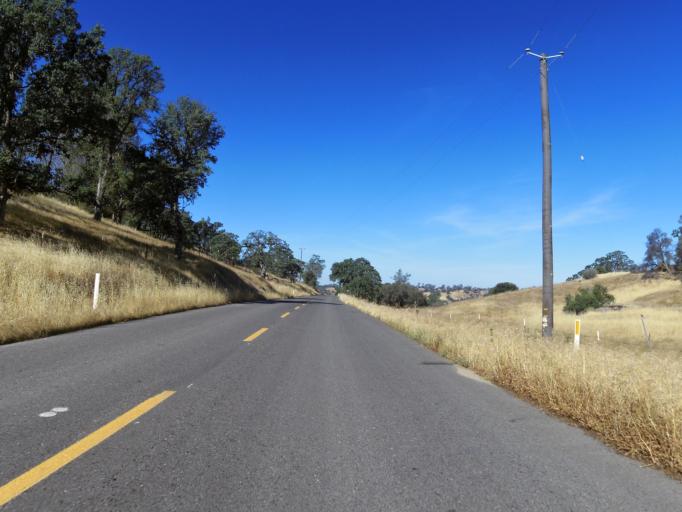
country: US
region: California
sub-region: Madera County
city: Yosemite Lakes
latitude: 37.1641
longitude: -119.8431
